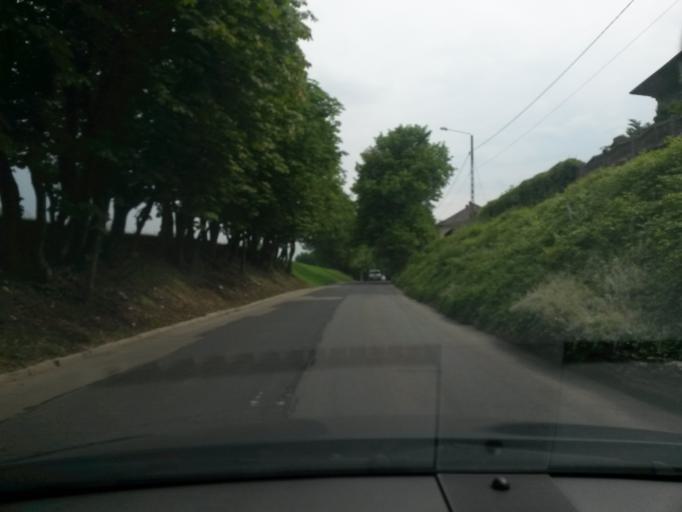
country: PL
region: Silesian Voivodeship
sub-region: Powiat czestochowski
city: Huta Stara B
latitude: 50.7644
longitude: 19.1540
